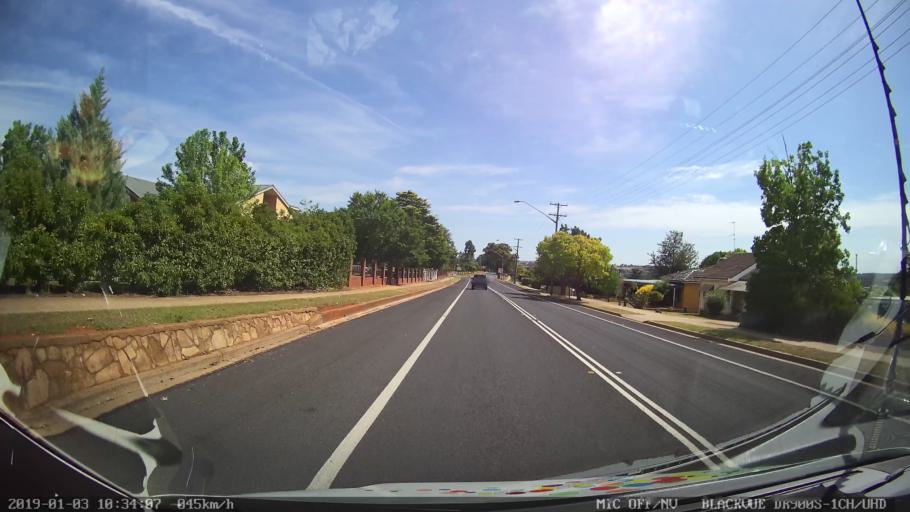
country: AU
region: New South Wales
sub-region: Young
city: Young
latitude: -34.3237
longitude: 148.2907
